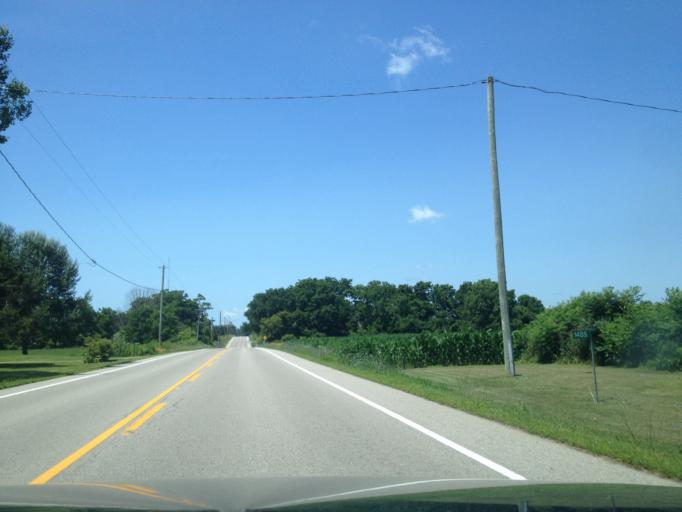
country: CA
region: Ontario
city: Norfolk County
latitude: 42.5825
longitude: -80.5946
